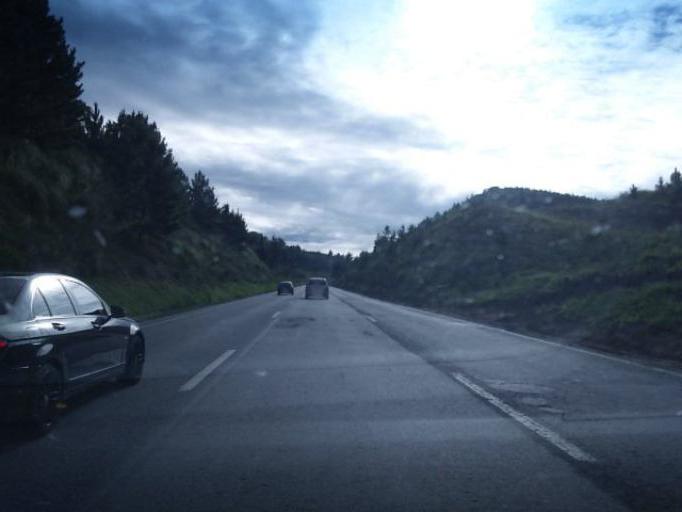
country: BR
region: Parana
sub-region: Campina Grande Do Sul
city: Campina Grande do Sul
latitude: -25.1026
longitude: -48.8338
